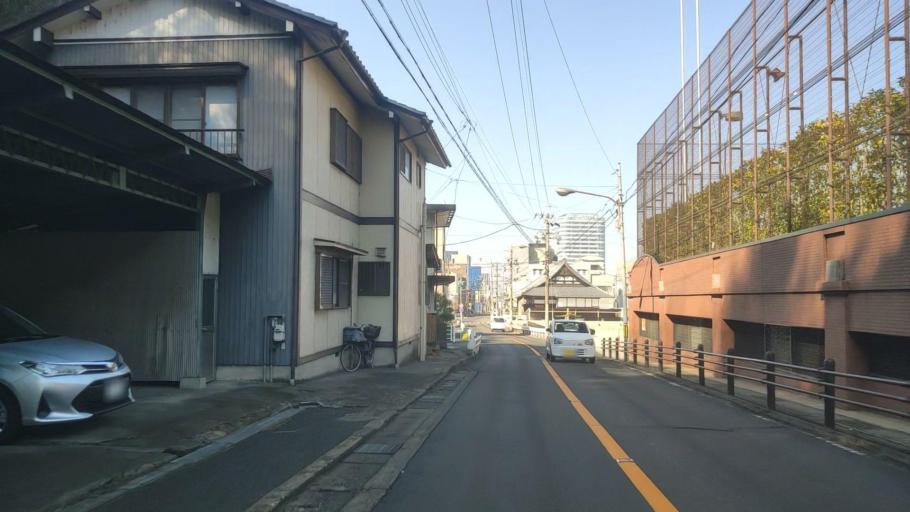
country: JP
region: Gifu
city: Gifu-shi
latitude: 35.4240
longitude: 136.7667
